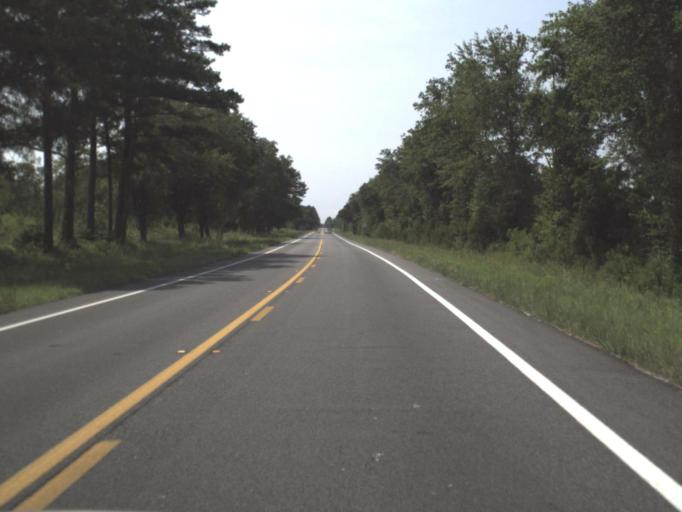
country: US
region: Georgia
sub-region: Echols County
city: Statenville
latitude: 30.6097
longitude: -83.0210
